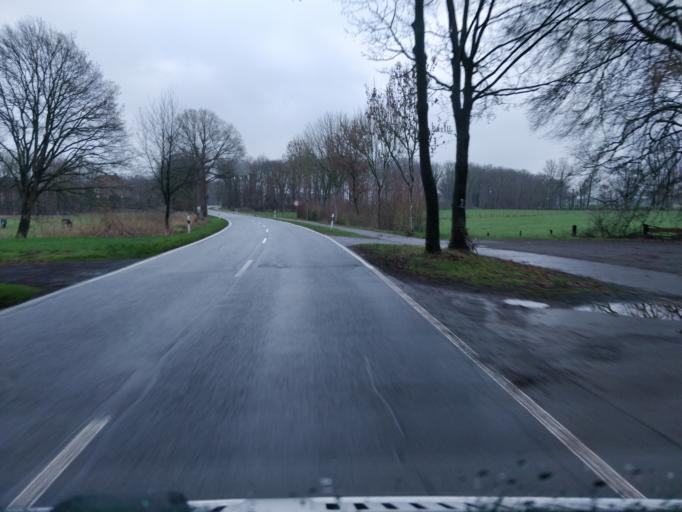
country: DE
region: North Rhine-Westphalia
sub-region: Regierungsbezirk Dusseldorf
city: Mehrhoog
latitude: 51.7633
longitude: 6.4854
